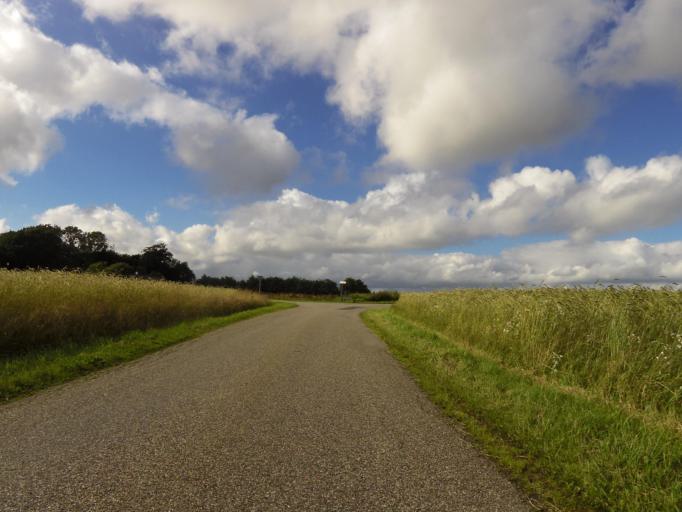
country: DK
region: South Denmark
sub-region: Tonder Kommune
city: Toftlund
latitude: 55.1346
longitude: 9.0720
